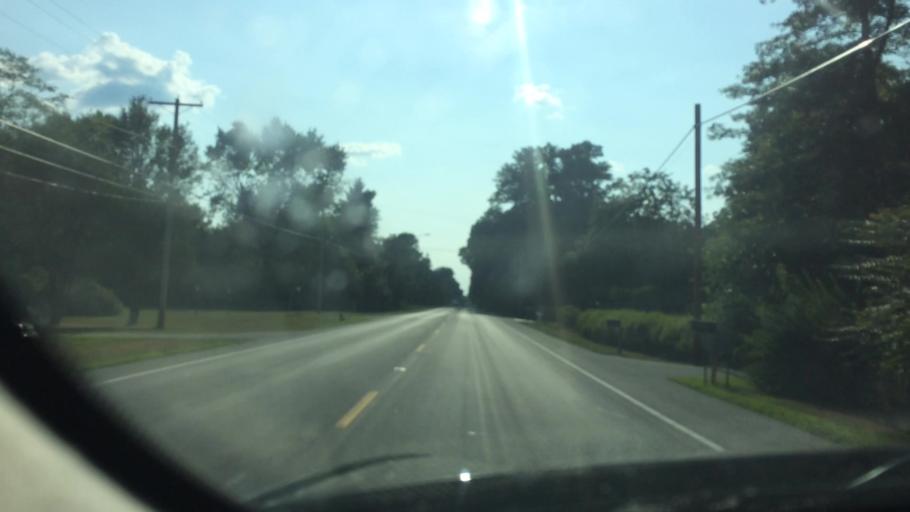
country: US
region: Ohio
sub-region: Lucas County
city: Holland
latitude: 41.6539
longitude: -83.7163
